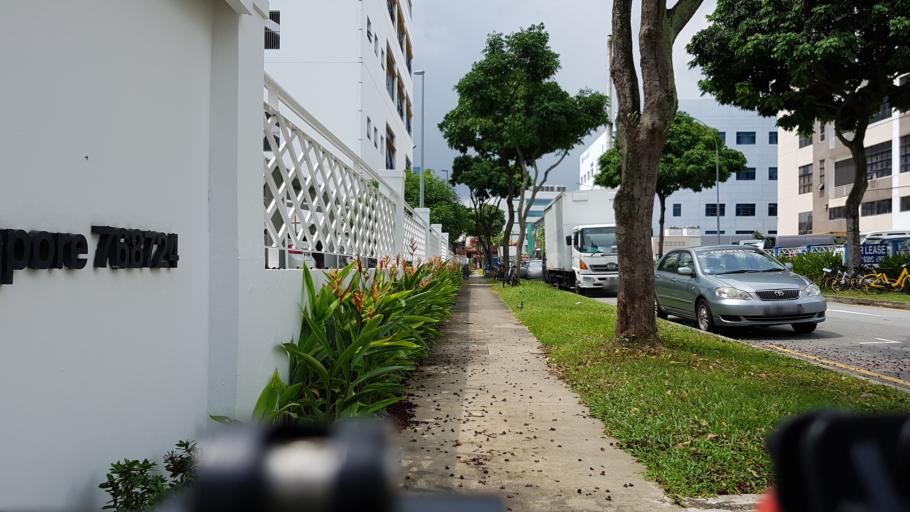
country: MY
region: Johor
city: Kampung Pasir Gudang Baru
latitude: 1.4423
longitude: 103.8343
